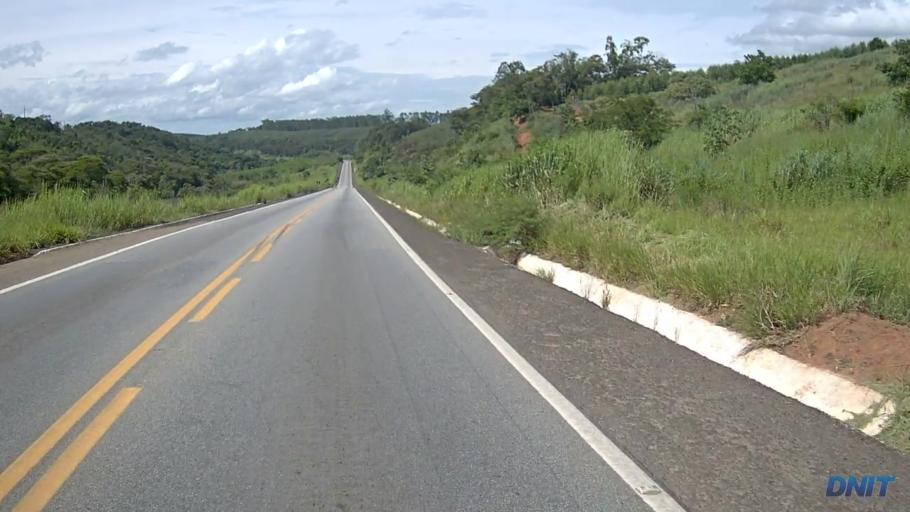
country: BR
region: Minas Gerais
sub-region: Ipatinga
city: Ipatinga
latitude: -19.4139
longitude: -42.4911
